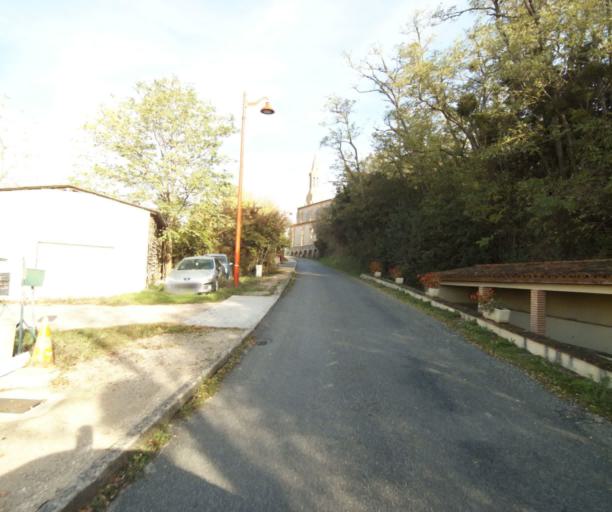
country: FR
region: Midi-Pyrenees
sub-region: Departement de la Haute-Garonne
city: Villemur-sur-Tarn
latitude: 43.9002
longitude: 1.4973
